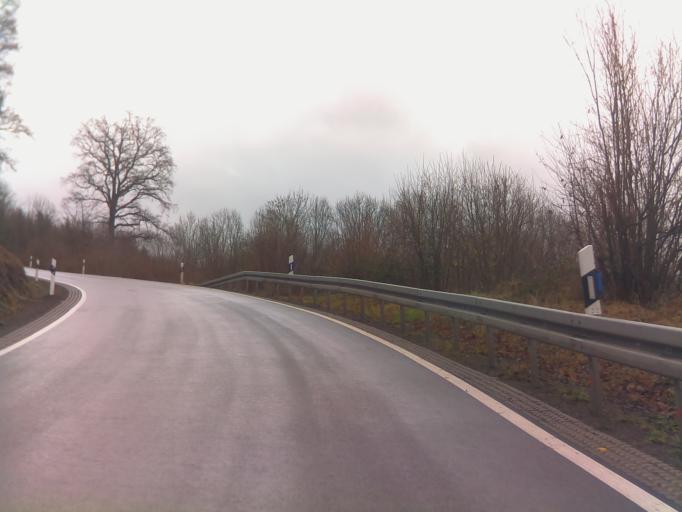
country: DE
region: Hesse
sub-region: Regierungsbezirk Giessen
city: Ulrichstein
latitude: 50.5809
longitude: 9.1490
